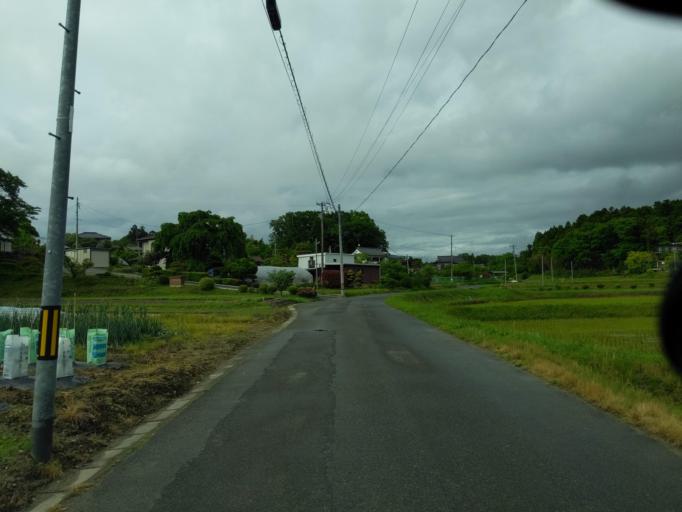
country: JP
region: Fukushima
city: Koriyama
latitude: 37.3612
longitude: 140.4151
